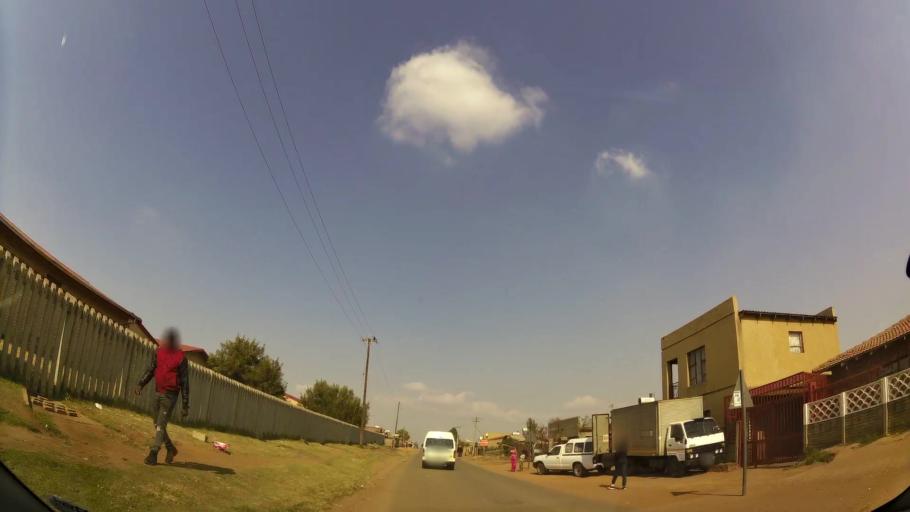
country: ZA
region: Gauteng
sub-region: Ekurhuleni Metropolitan Municipality
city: Springs
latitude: -26.1140
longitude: 28.4808
